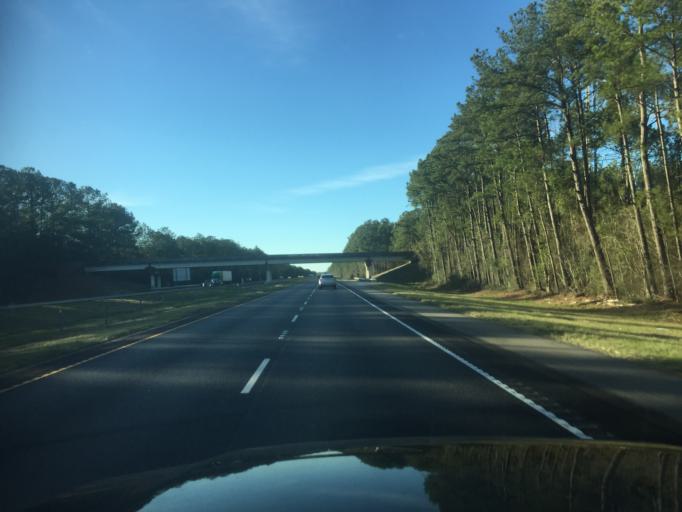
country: US
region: Louisiana
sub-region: Saint Tammany Parish
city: Lacombe
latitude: 30.3608
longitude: -89.9364
